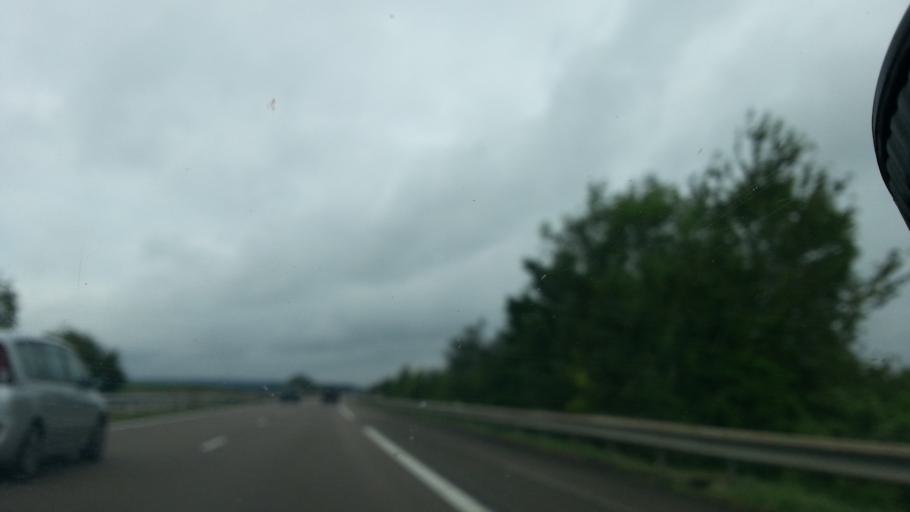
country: FR
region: Franche-Comte
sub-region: Departement du Jura
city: Dole
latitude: 47.1366
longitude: 5.5357
